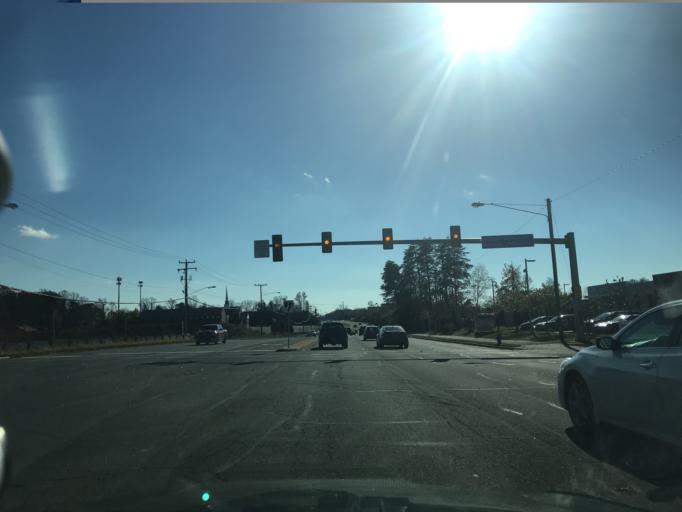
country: US
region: Virginia
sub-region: Fairfax County
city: Greenbriar
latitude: 38.8567
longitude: -77.3717
